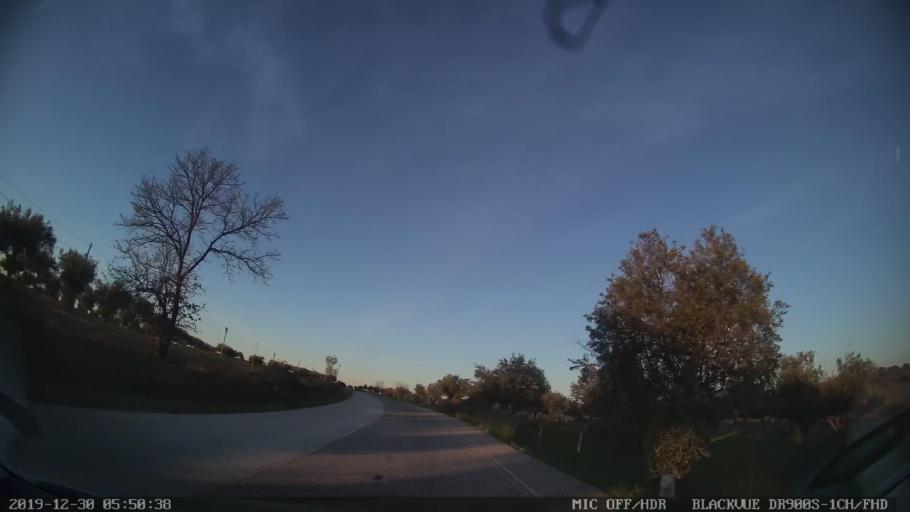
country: PT
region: Castelo Branco
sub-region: Idanha-A-Nova
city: Idanha-a-Nova
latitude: 39.9861
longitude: -7.2420
